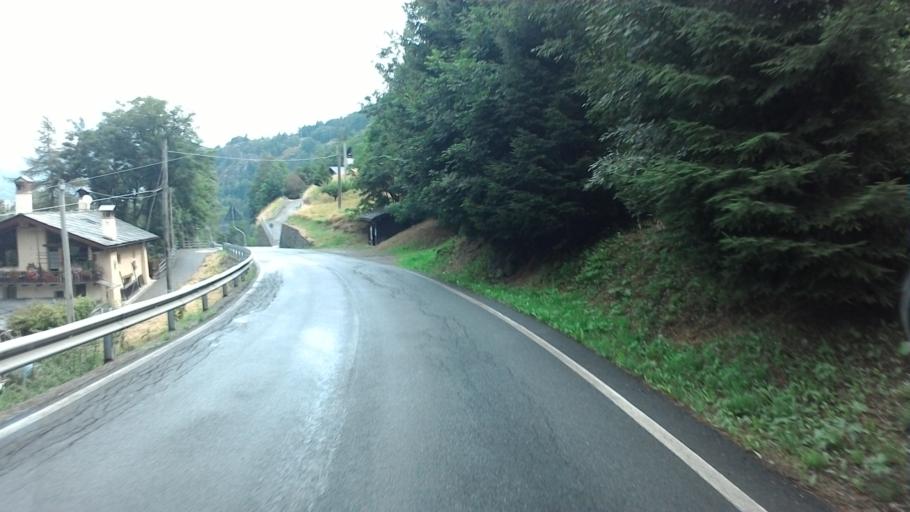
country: IT
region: Aosta Valley
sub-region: Valle d'Aosta
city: Plan d'Introd
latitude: 45.6711
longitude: 7.1727
